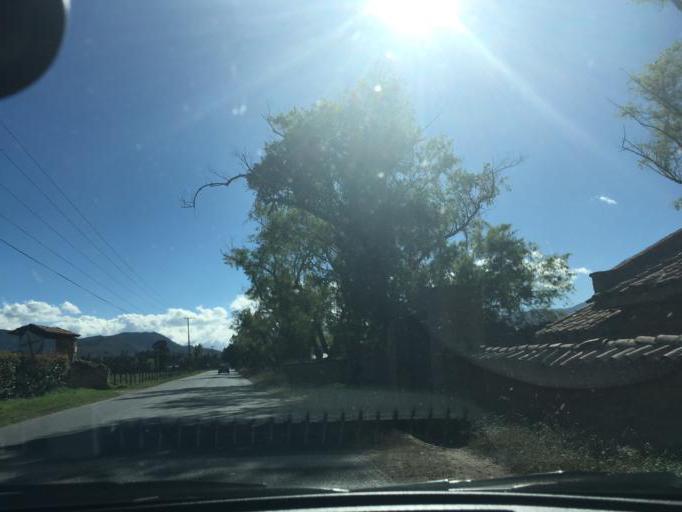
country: CO
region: Boyaca
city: Firavitoba
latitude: 5.6513
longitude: -72.9847
